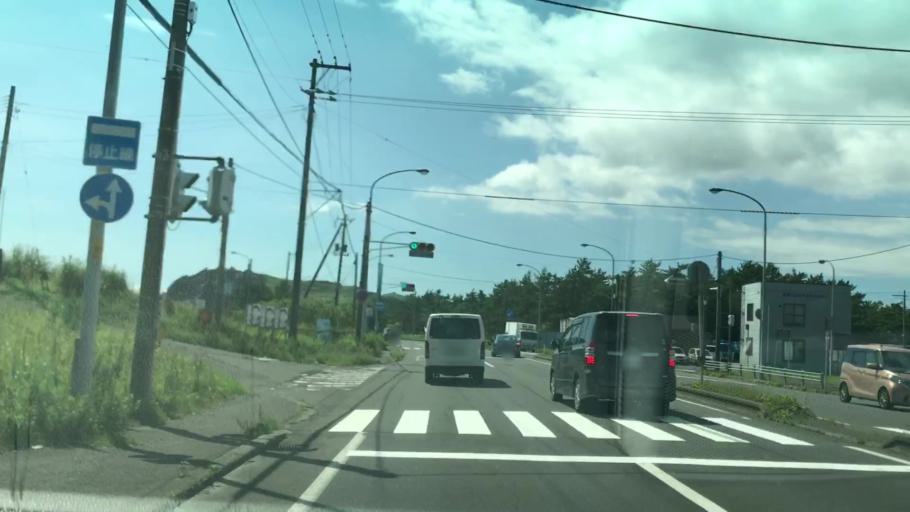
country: JP
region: Hokkaido
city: Muroran
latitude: 42.3483
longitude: 141.0396
